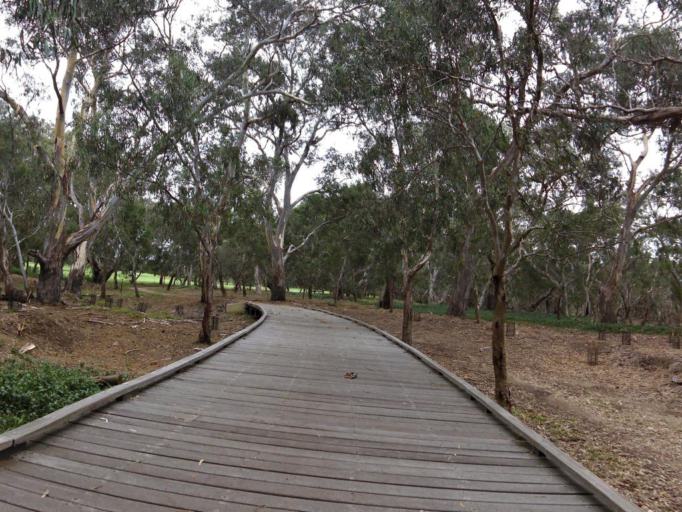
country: AU
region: Victoria
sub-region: Wyndham
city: Werribee
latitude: -37.9328
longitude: 144.6654
